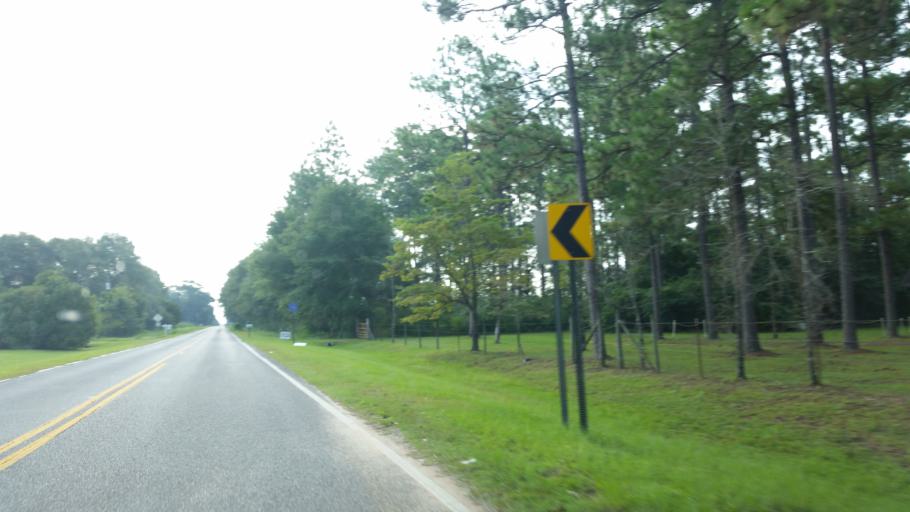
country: US
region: Florida
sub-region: Escambia County
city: Molino
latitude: 30.7711
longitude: -87.5230
